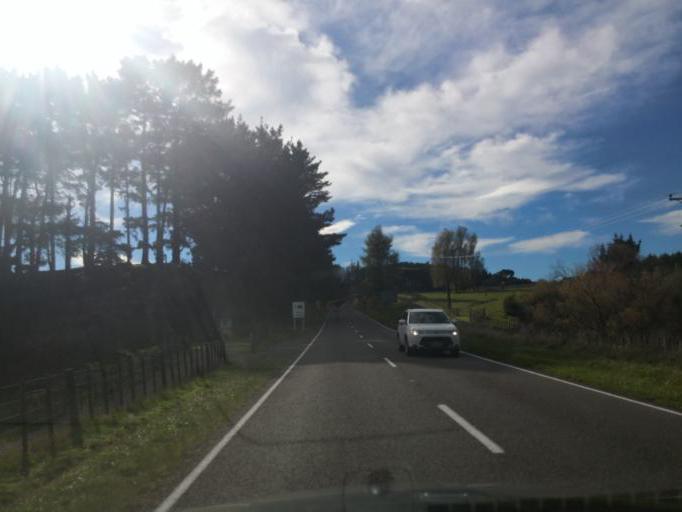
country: NZ
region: Manawatu-Wanganui
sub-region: Palmerston North City
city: Palmerston North
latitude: -40.3933
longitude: 175.6337
